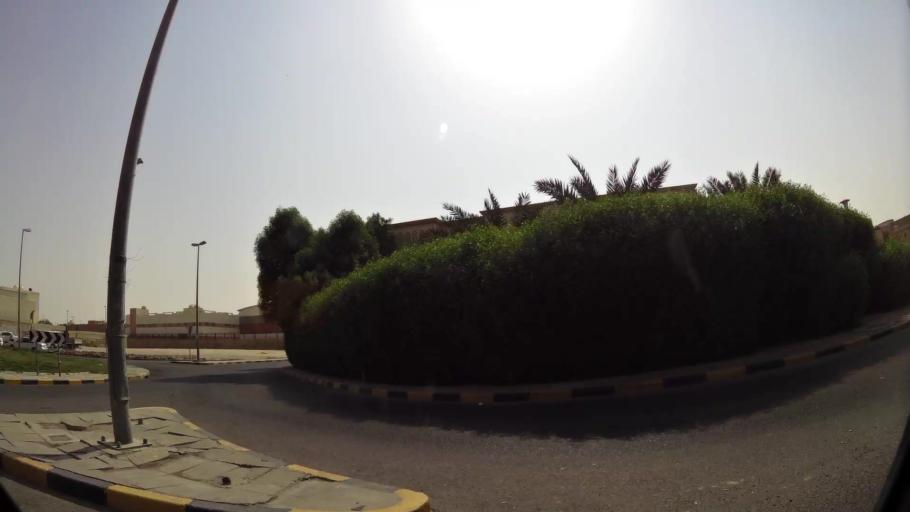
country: KW
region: Muhafazat al Jahra'
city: Al Jahra'
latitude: 29.3237
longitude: 47.6695
